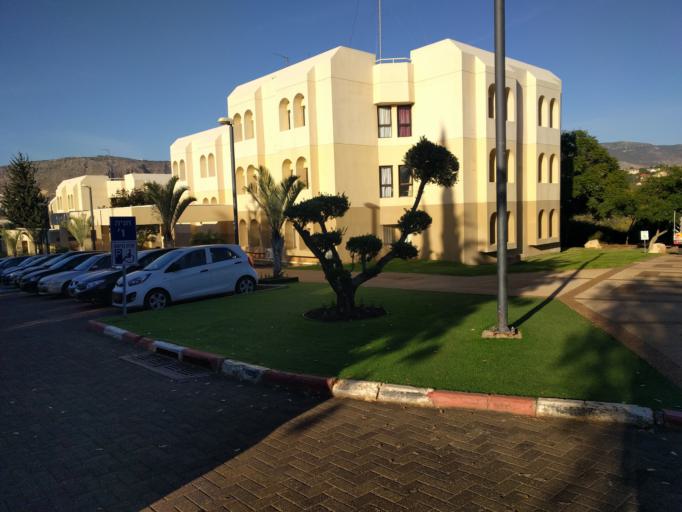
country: IL
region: Northern District
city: Karmi'el
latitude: 32.9139
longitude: 35.2839
